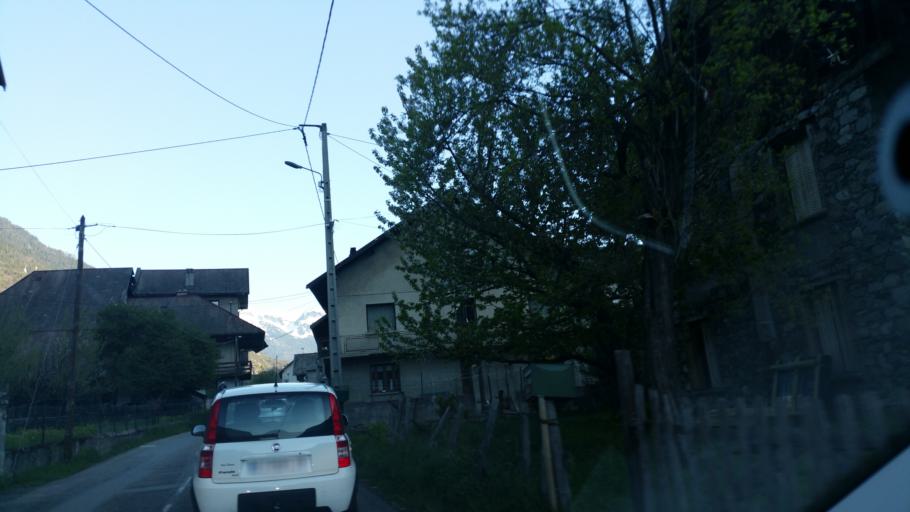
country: FR
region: Rhone-Alpes
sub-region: Departement de la Savoie
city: La Chambre
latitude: 45.3382
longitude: 6.3023
